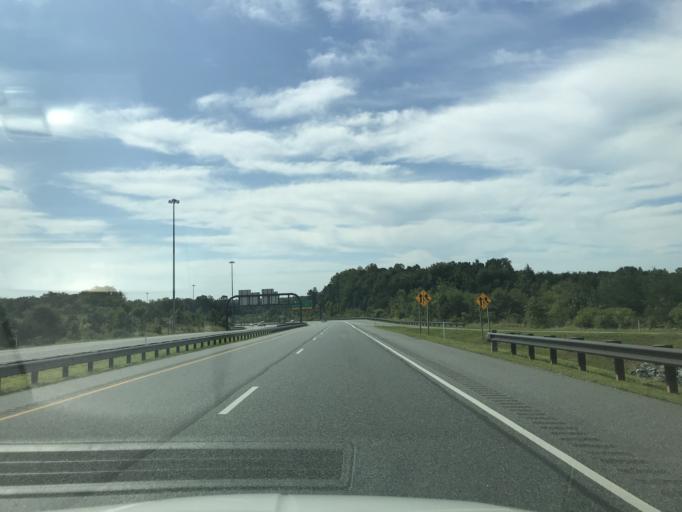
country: US
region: Maryland
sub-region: Prince George's County
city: West Laurel
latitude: 39.0706
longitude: -76.9029
